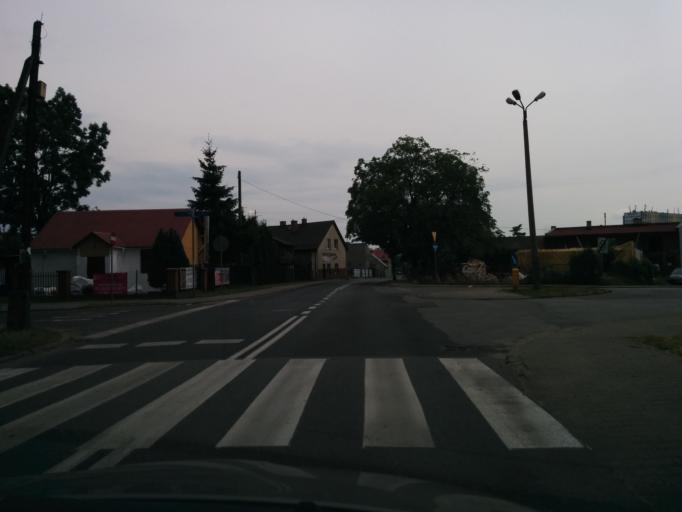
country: PL
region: Silesian Voivodeship
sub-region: Ruda Slaska
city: Ruda Slaska
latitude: 50.2439
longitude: 18.8379
